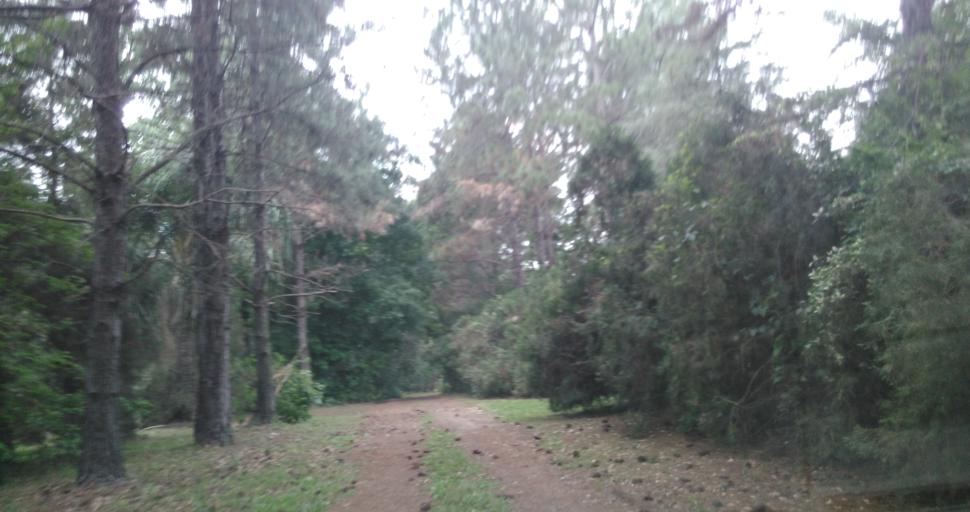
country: AR
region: Chaco
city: Fontana
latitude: -27.4031
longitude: -59.0101
